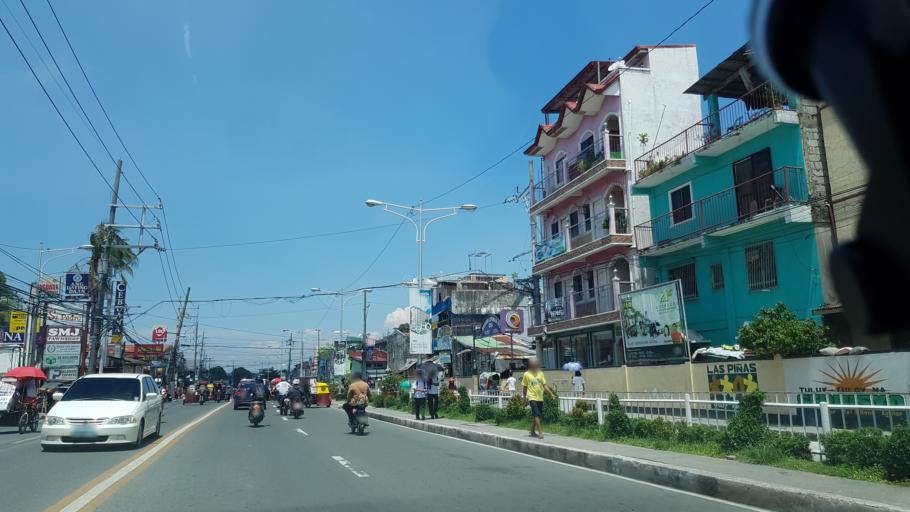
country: PH
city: Sambayanihan People's Village
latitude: 14.4594
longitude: 120.9947
